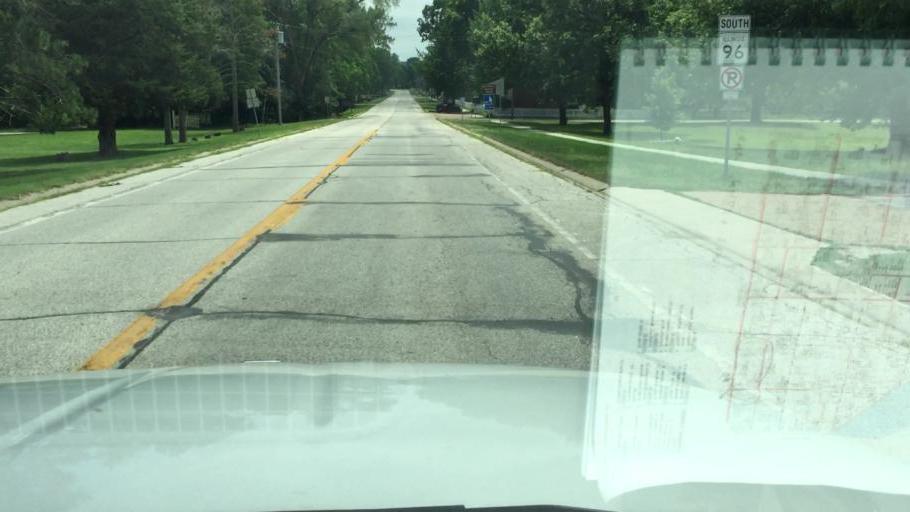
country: US
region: Illinois
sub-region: Hancock County
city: Nauvoo
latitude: 40.5473
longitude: -91.3866
